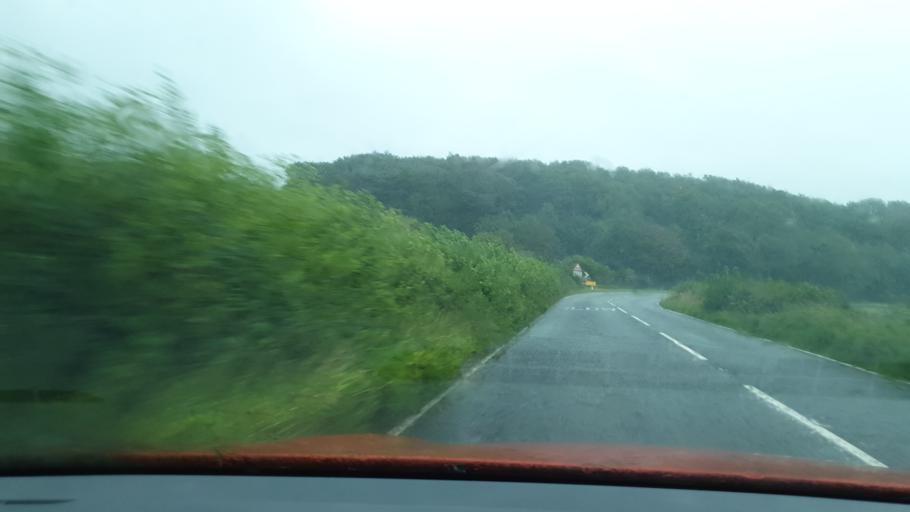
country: GB
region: England
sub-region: Cumbria
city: Millom
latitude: 54.2697
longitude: -3.2177
